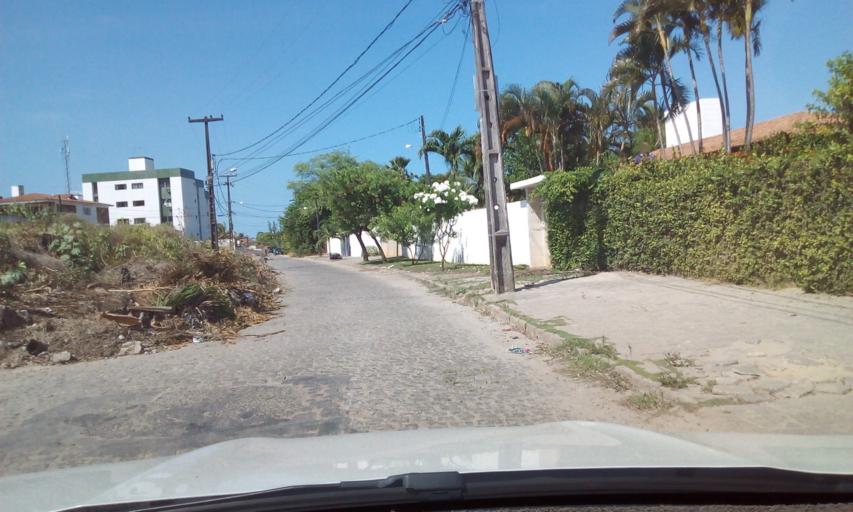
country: BR
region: Paraiba
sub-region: Joao Pessoa
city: Joao Pessoa
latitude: -7.1603
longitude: -34.8462
